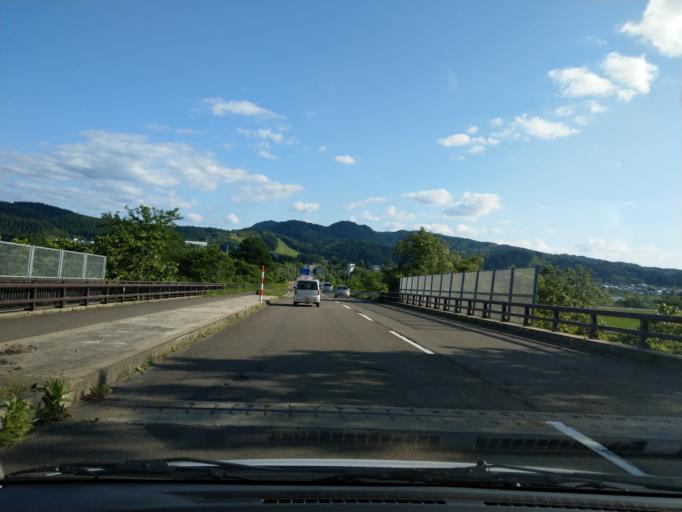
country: JP
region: Akita
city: Takanosu
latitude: 40.1298
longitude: 140.3812
